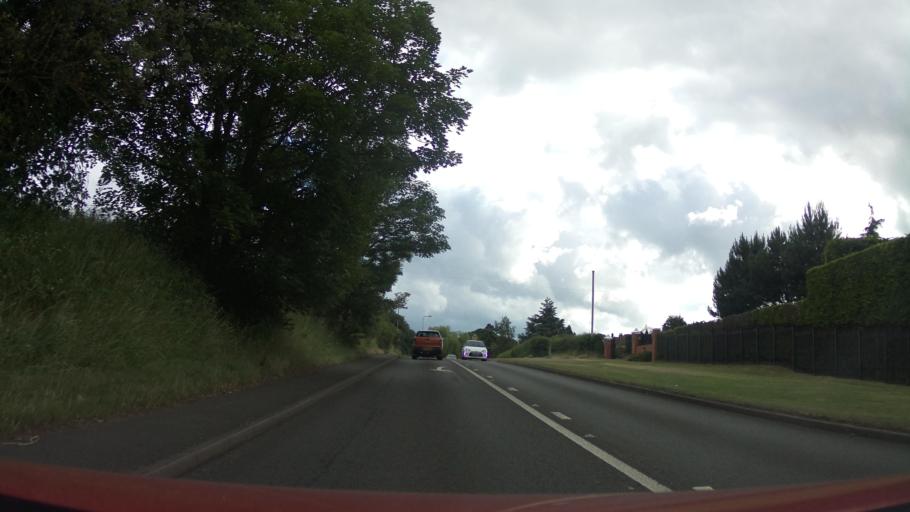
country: GB
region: England
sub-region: Dudley
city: Kingswinford
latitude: 52.4662
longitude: -2.1991
